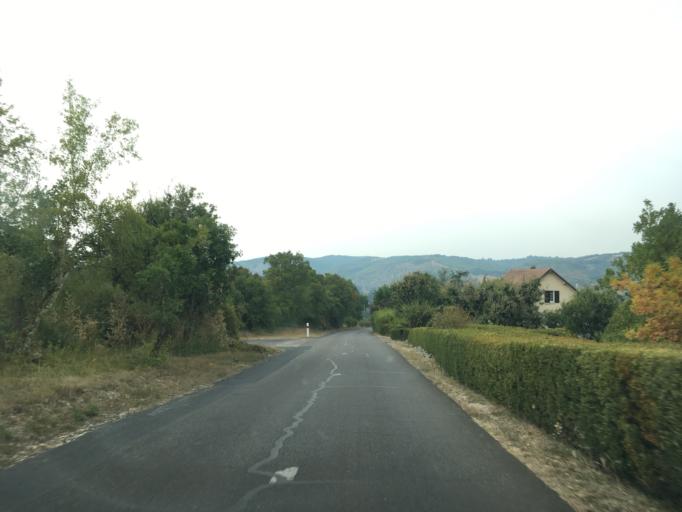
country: FR
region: Midi-Pyrenees
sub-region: Departement du Lot
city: Souillac
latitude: 44.8400
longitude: 1.5589
